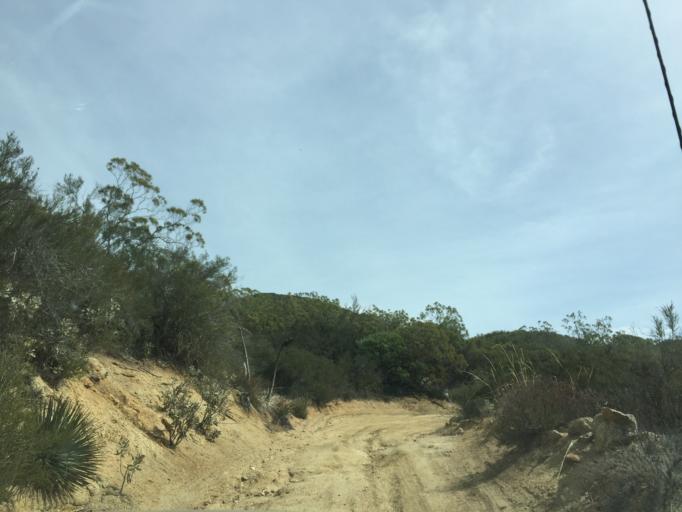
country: US
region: California
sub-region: Riverside County
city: Valle Vista
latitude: 33.6209
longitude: -116.8200
